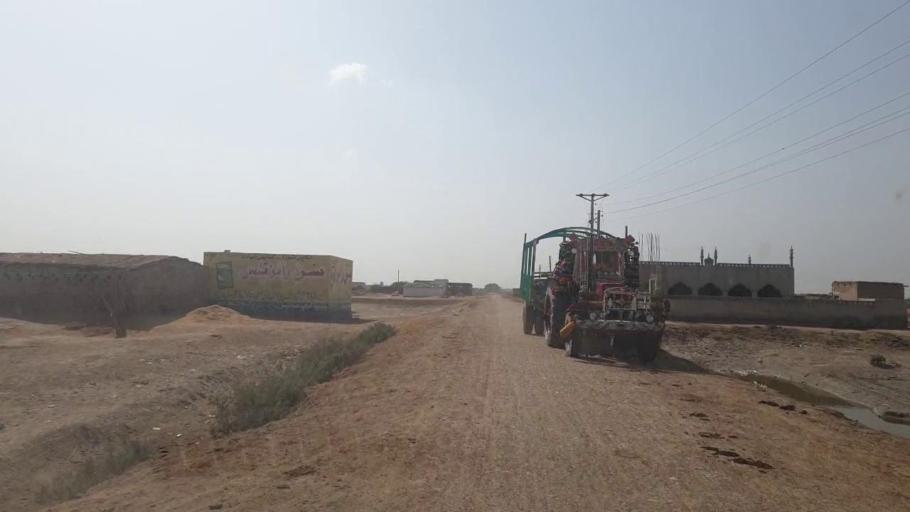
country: PK
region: Sindh
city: Kario
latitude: 24.5150
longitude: 68.5252
